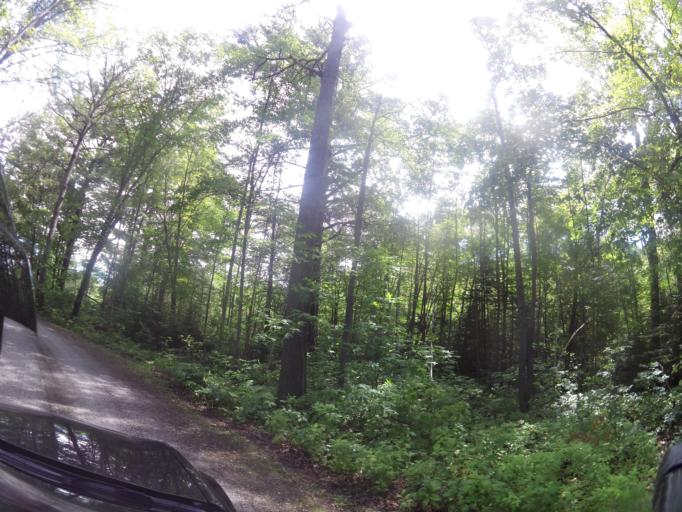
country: CA
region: Ontario
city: Elliot Lake
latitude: 46.2102
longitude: -82.5136
